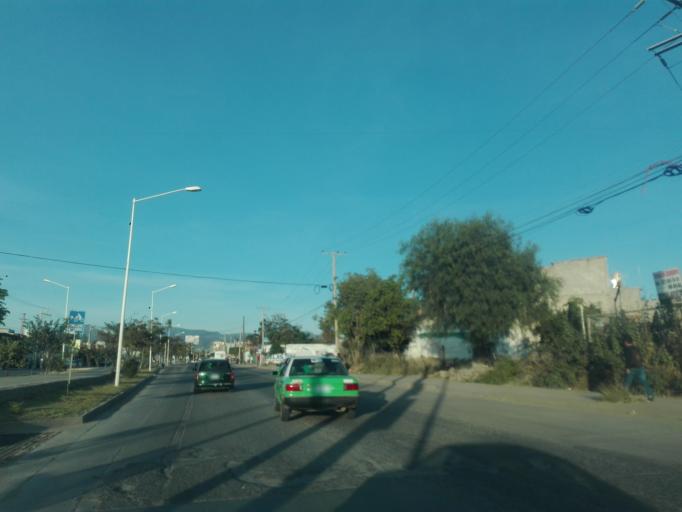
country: MX
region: Guanajuato
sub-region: Leon
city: San Jose de Duran (Los Troncoso)
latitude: 21.0767
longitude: -101.6351
